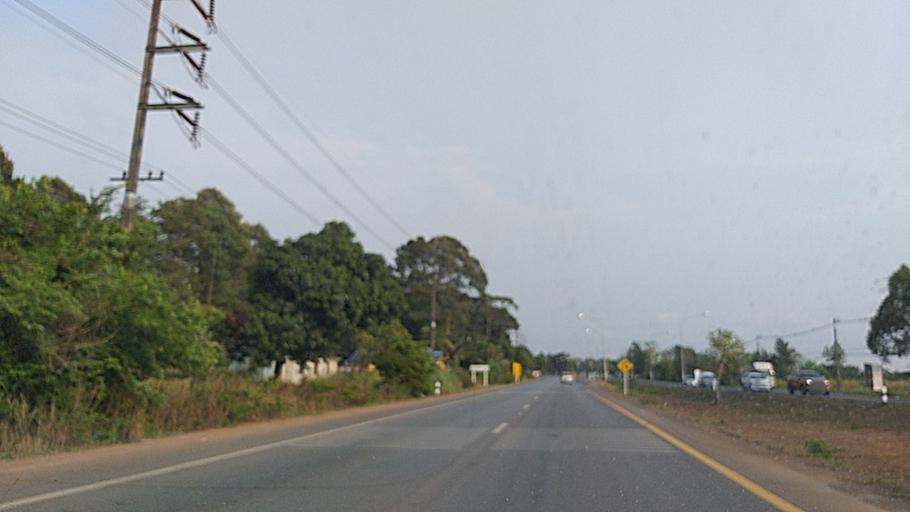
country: TH
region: Chanthaburi
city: Khlung
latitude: 12.4344
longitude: 102.3081
